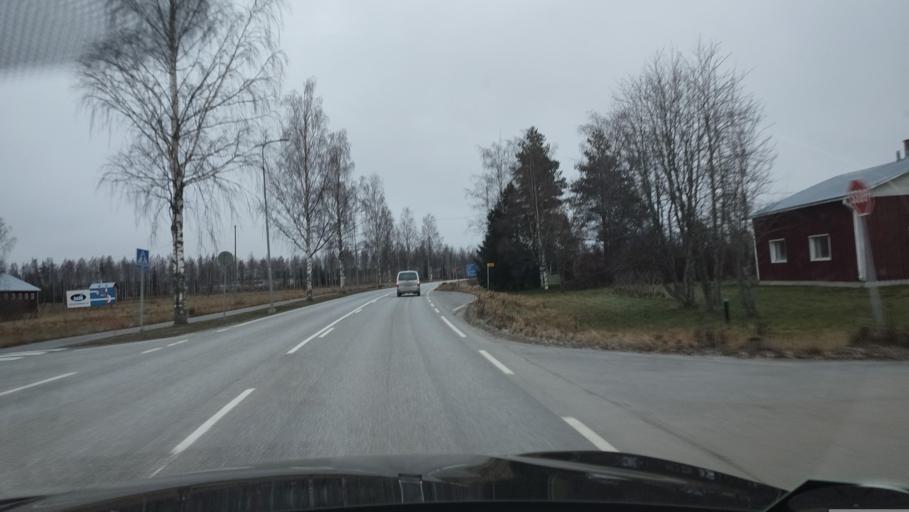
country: FI
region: Southern Ostrobothnia
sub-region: Suupohja
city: Kauhajoki
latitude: 62.4526
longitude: 22.2033
